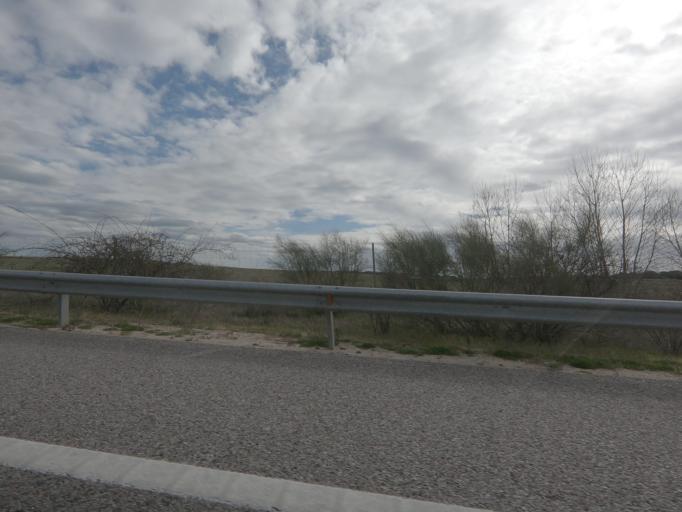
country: ES
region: Castille and Leon
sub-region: Provincia de Salamanca
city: Carpio de Azaba
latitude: 40.5855
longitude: -6.6013
